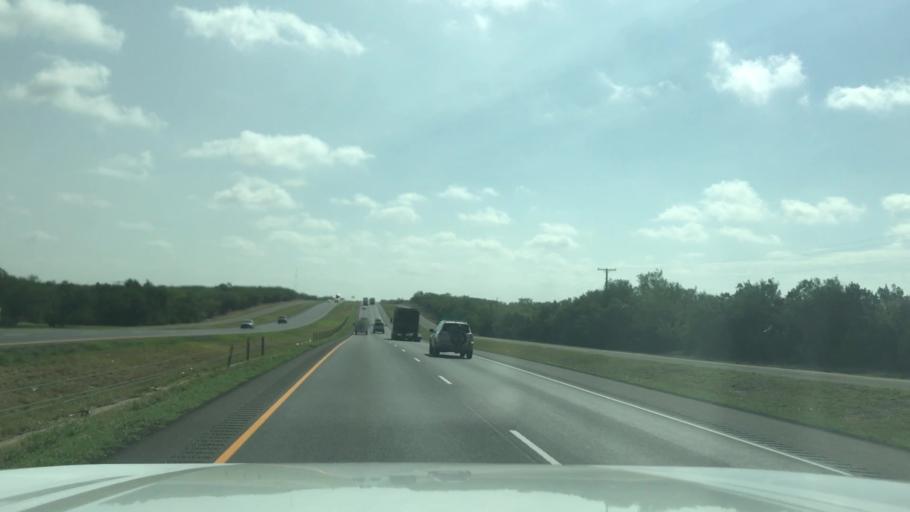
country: US
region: Texas
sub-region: Nolan County
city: Sweetwater
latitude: 32.4901
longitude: -100.3270
